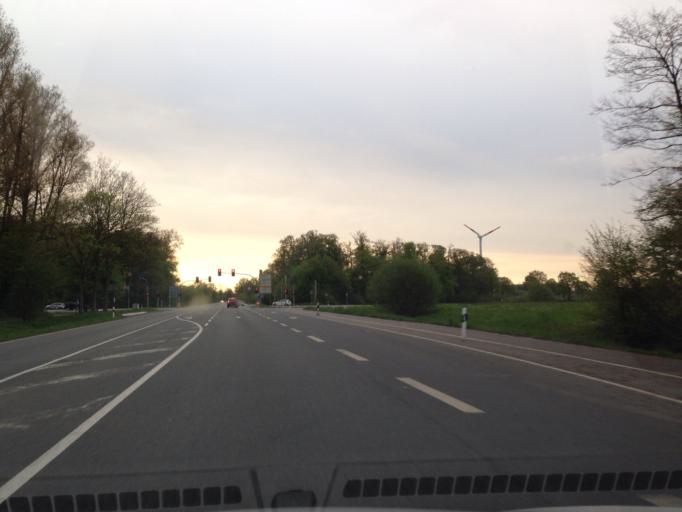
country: DE
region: North Rhine-Westphalia
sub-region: Regierungsbezirk Munster
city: Altenberge
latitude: 52.0714
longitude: 7.4388
